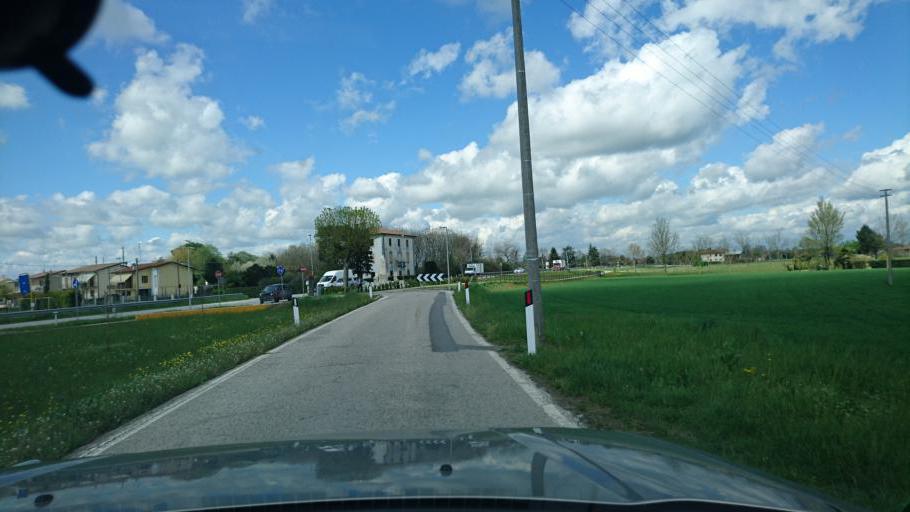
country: IT
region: Veneto
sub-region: Provincia di Padova
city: Tremignon
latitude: 45.5237
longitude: 11.7993
